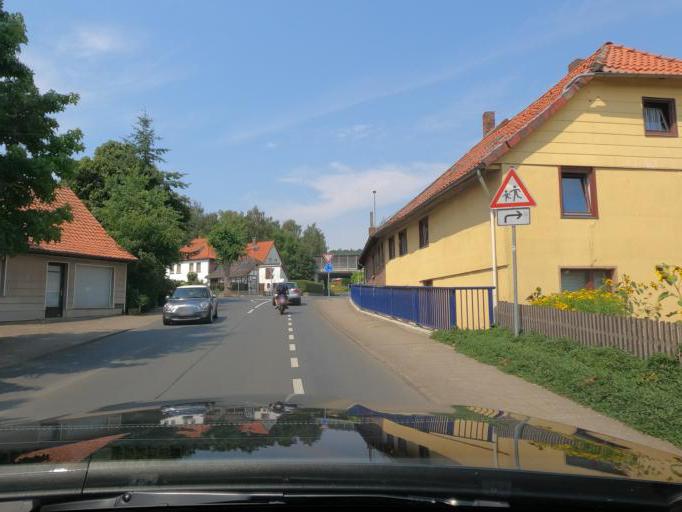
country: DE
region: Lower Saxony
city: Springe
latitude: 52.2186
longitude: 9.6225
